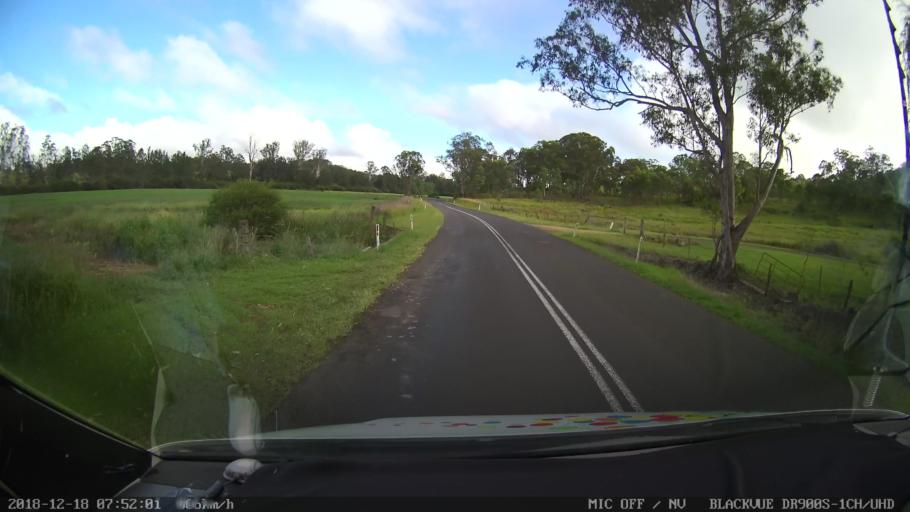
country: AU
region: New South Wales
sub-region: Kyogle
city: Kyogle
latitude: -28.4327
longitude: 152.5809
